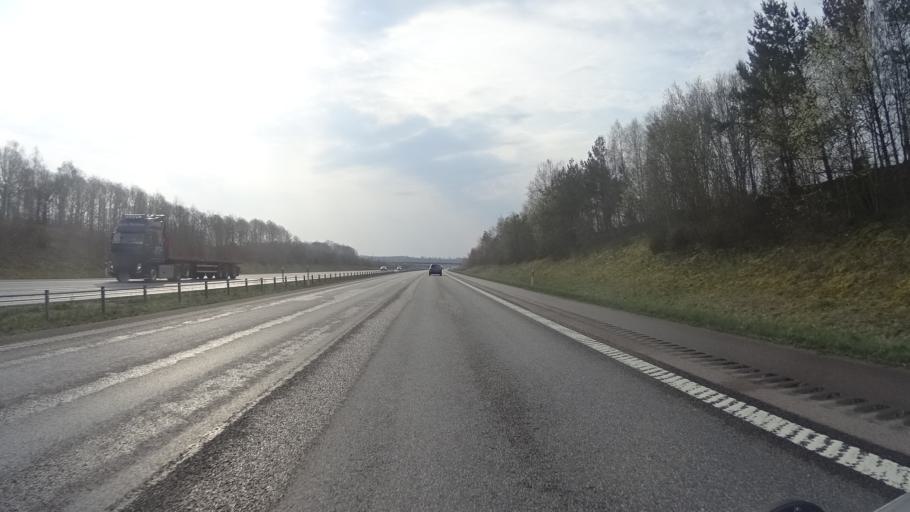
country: SE
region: Halland
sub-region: Halmstads Kommun
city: Aled
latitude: 56.7468
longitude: 12.8617
